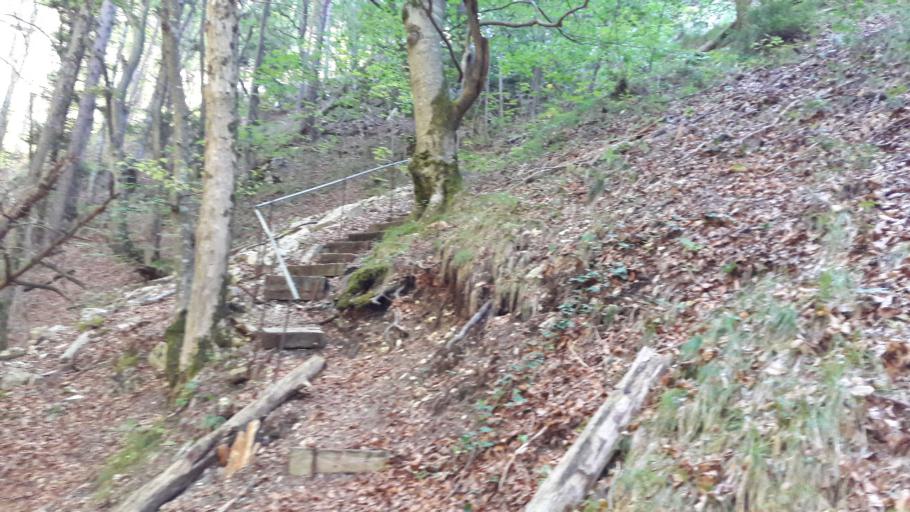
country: CH
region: Solothurn
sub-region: Bezirk Thal
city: Laupersdorf
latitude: 47.3272
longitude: 7.6509
